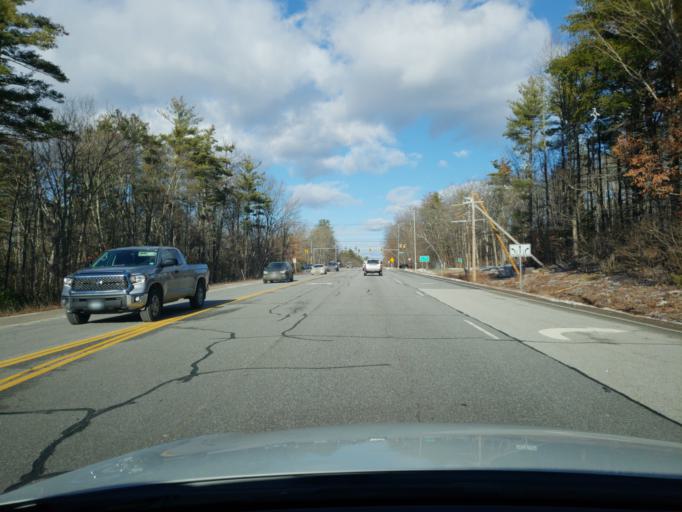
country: US
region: New Hampshire
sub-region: Hillsborough County
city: Pinardville
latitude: 42.9888
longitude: -71.5231
